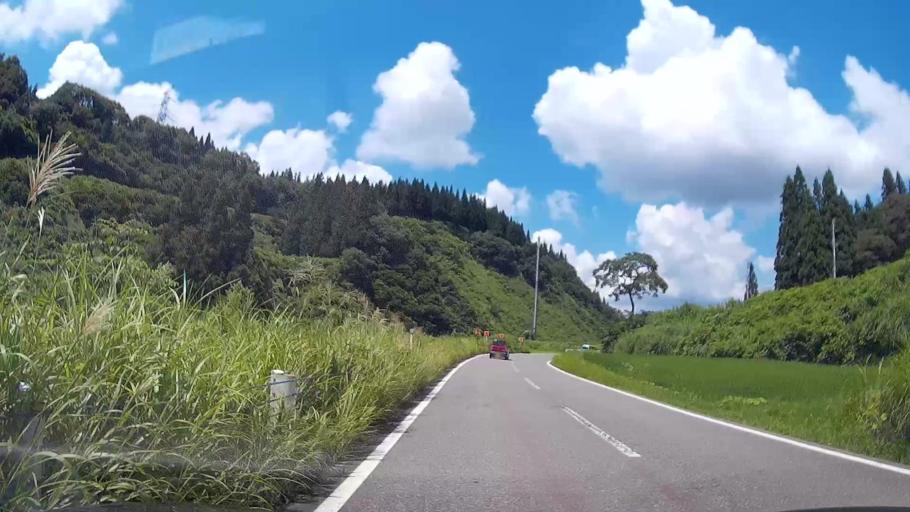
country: JP
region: Niigata
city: Tokamachi
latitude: 37.0525
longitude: 138.7609
